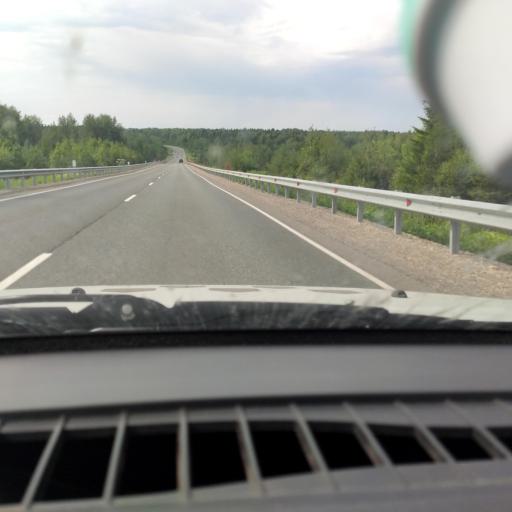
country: RU
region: Kirov
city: Omutninsk
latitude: 58.6903
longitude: 52.1325
